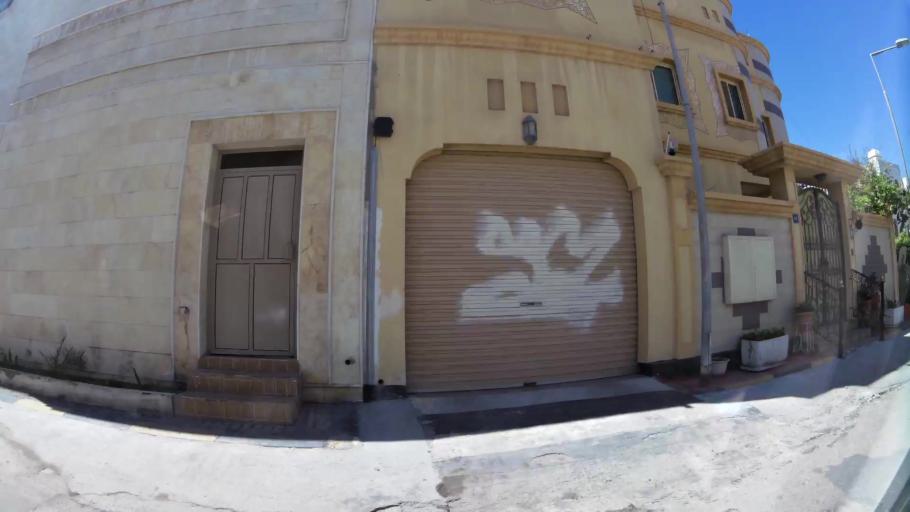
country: BH
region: Muharraq
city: Al Muharraq
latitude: 26.2826
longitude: 50.6243
